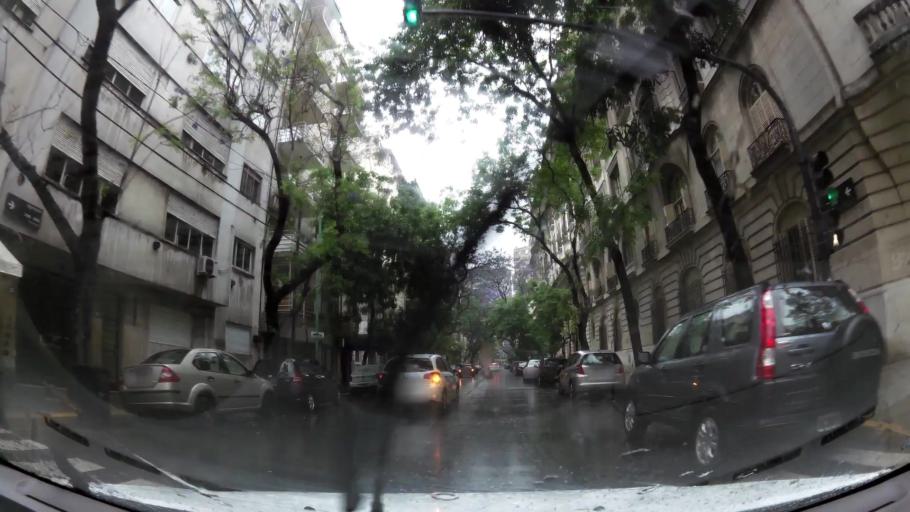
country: AR
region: Buenos Aires F.D.
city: Retiro
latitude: -34.5804
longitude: -58.4119
